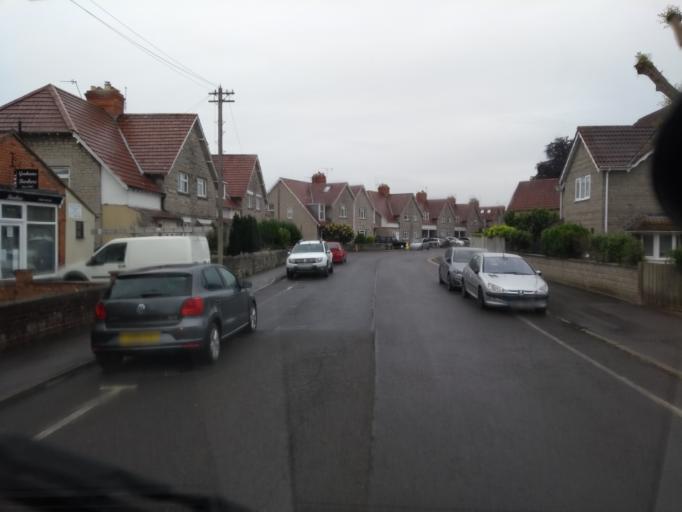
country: GB
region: England
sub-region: Somerset
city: Street
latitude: 51.1245
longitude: -2.7407
